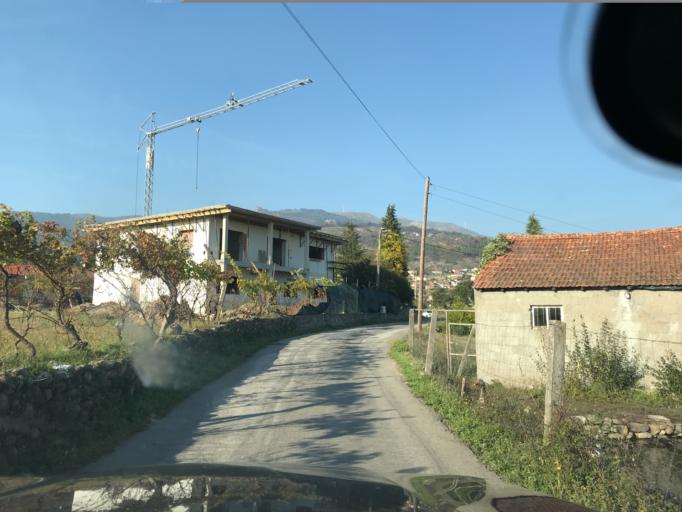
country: PT
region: Vila Real
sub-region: Vila Real
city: Vila Real
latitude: 41.3152
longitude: -7.7589
